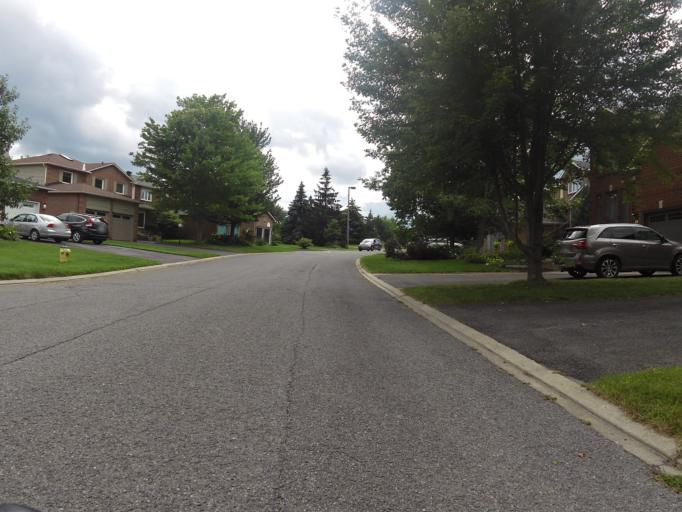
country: CA
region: Ontario
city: Bells Corners
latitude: 45.3210
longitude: -75.9077
